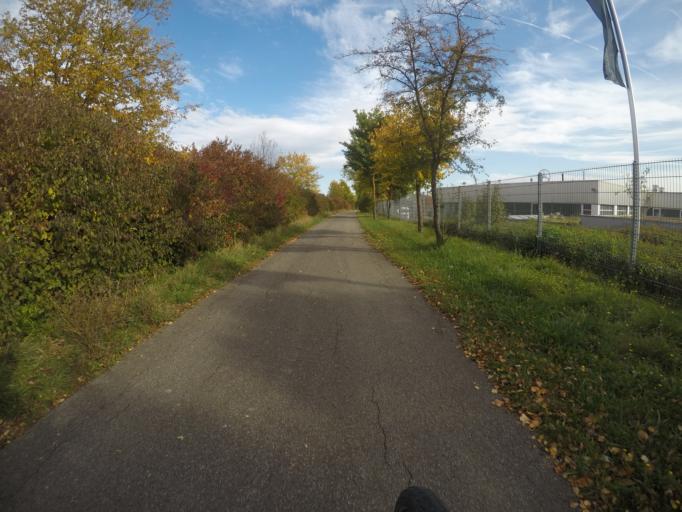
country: DE
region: Baden-Wuerttemberg
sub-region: Regierungsbezirk Stuttgart
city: Herrenberg
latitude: 48.5779
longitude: 8.8948
